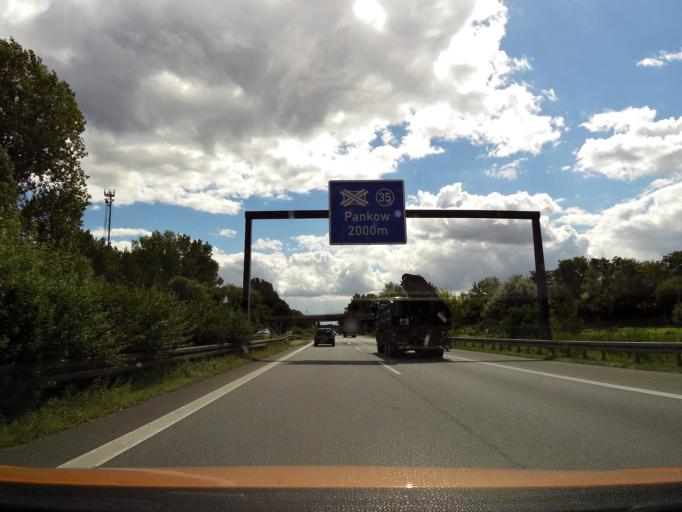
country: DE
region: Berlin
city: Blankenfelde
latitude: 52.6635
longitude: 13.4083
